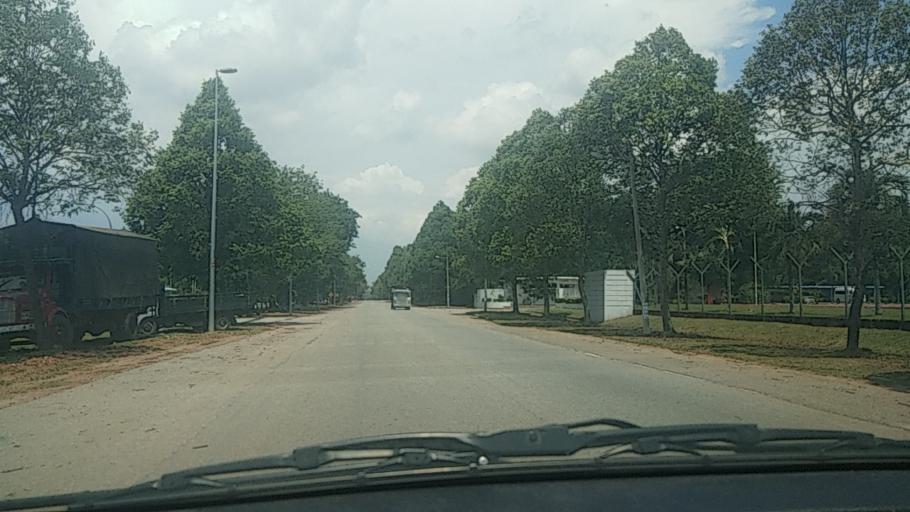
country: MY
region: Kedah
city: Sungai Petani
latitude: 5.6562
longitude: 100.5315
